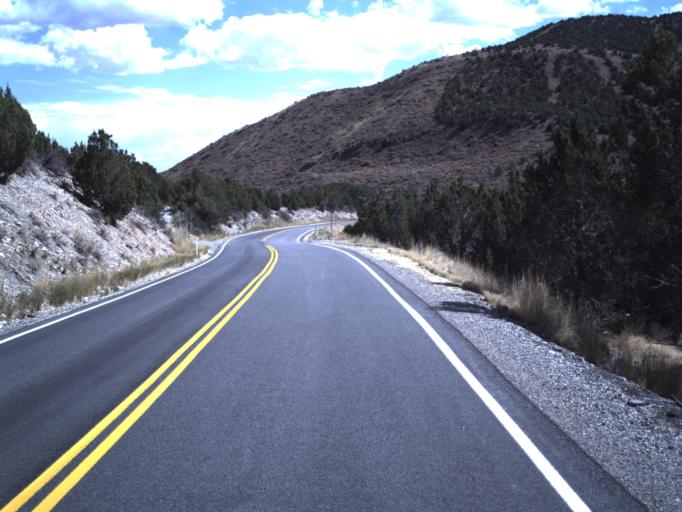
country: US
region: Utah
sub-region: Tooele County
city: Grantsville
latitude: 40.3479
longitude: -112.5506
